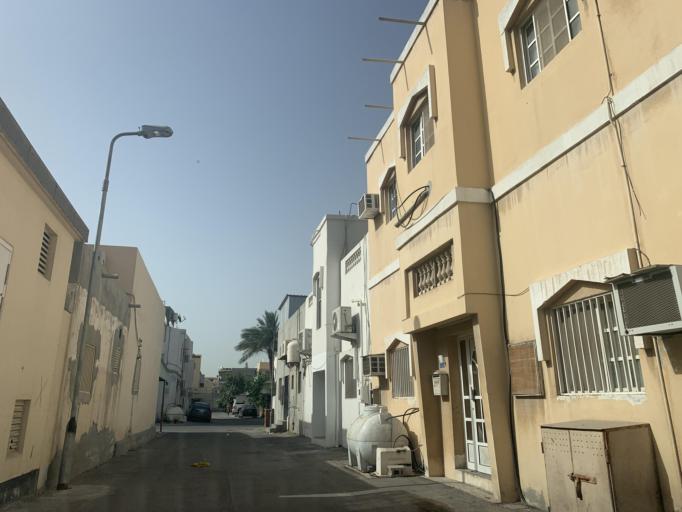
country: BH
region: Northern
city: Sitrah
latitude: 26.1673
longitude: 50.6069
